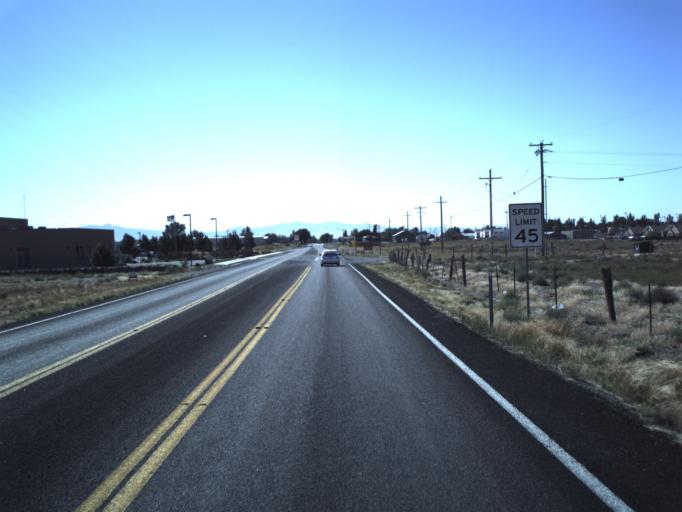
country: US
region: Utah
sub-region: Beaver County
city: Milford
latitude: 38.4089
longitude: -113.0099
